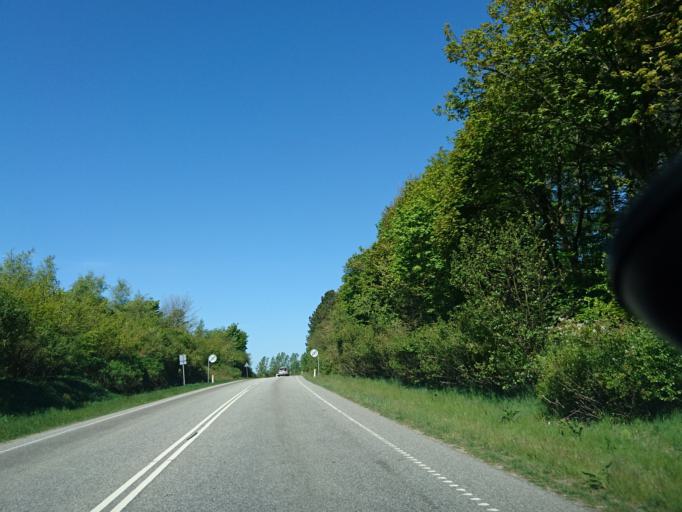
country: DK
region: North Denmark
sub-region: Hjorring Kommune
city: Sindal
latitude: 57.4608
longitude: 10.3074
